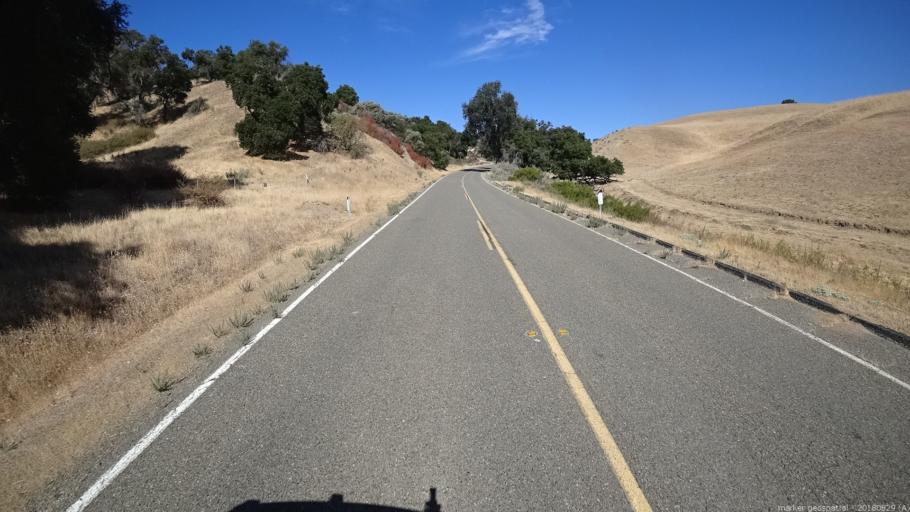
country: US
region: California
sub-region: San Luis Obispo County
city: Lake Nacimiento
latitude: 35.8404
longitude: -121.0429
